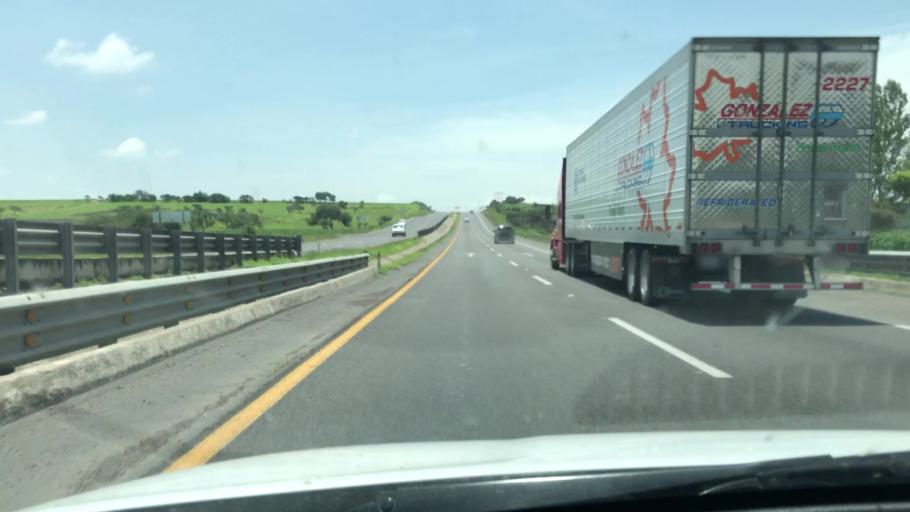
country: MX
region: Guanajuato
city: Penjamo
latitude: 20.3833
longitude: -101.8000
